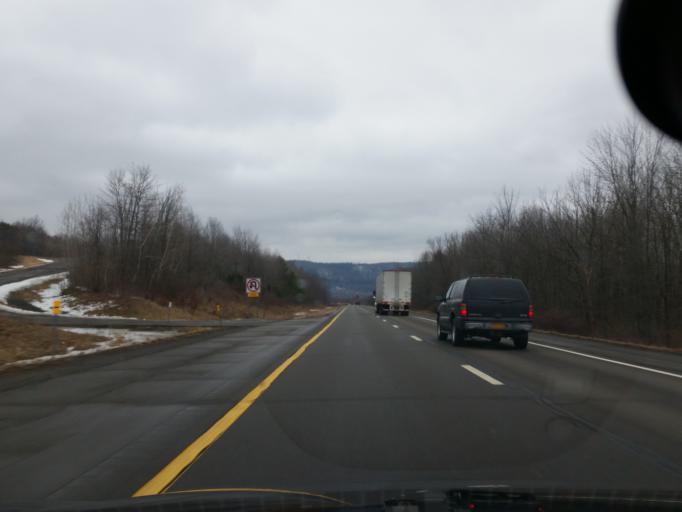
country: US
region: Pennsylvania
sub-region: Susquehanna County
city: Hallstead
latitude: 42.0310
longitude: -75.7880
